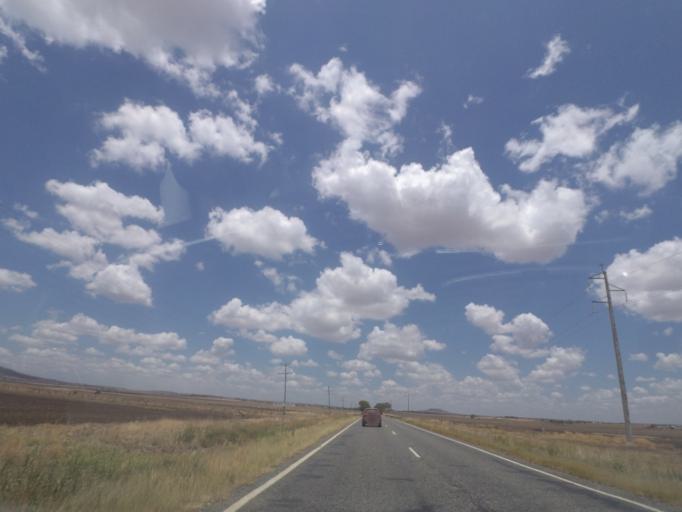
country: AU
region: Queensland
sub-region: Toowoomba
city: Top Camp
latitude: -27.9121
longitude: 151.9799
